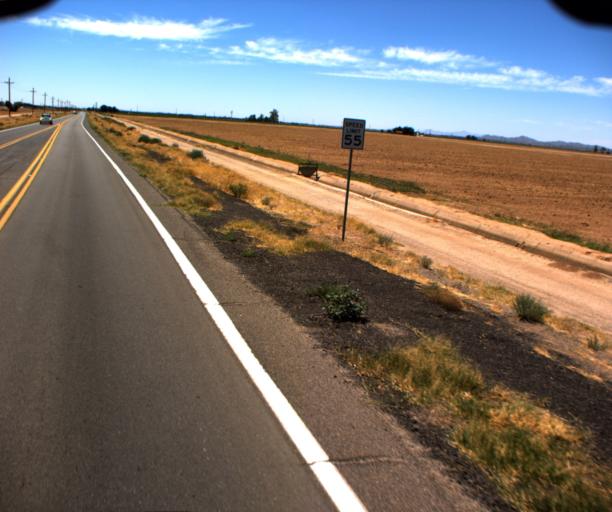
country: US
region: Arizona
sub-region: Pinal County
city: Casa Grande
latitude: 32.8798
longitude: -111.6546
